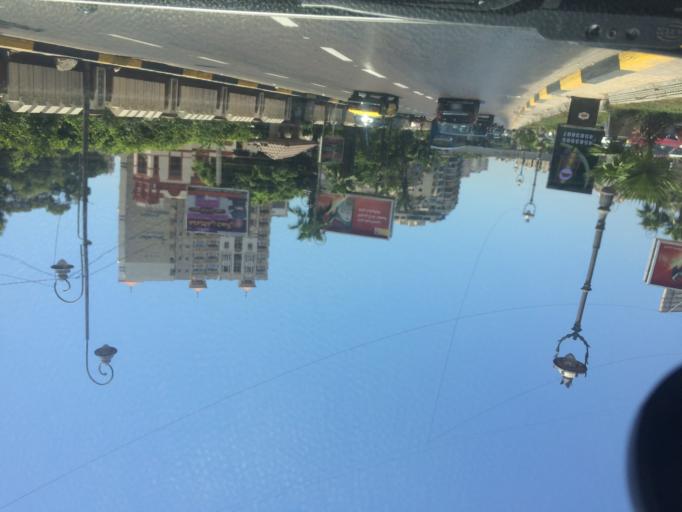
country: EG
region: Alexandria
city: Alexandria
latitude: 31.1966
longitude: 29.9181
